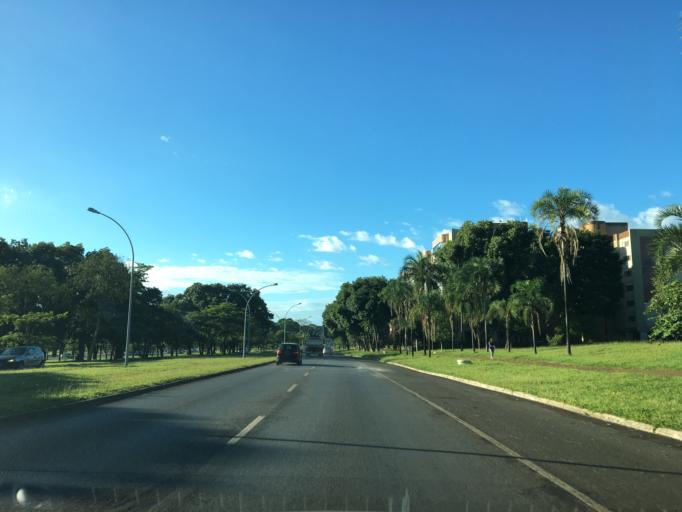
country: BR
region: Federal District
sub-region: Brasilia
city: Brasilia
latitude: -15.7486
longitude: -47.8892
